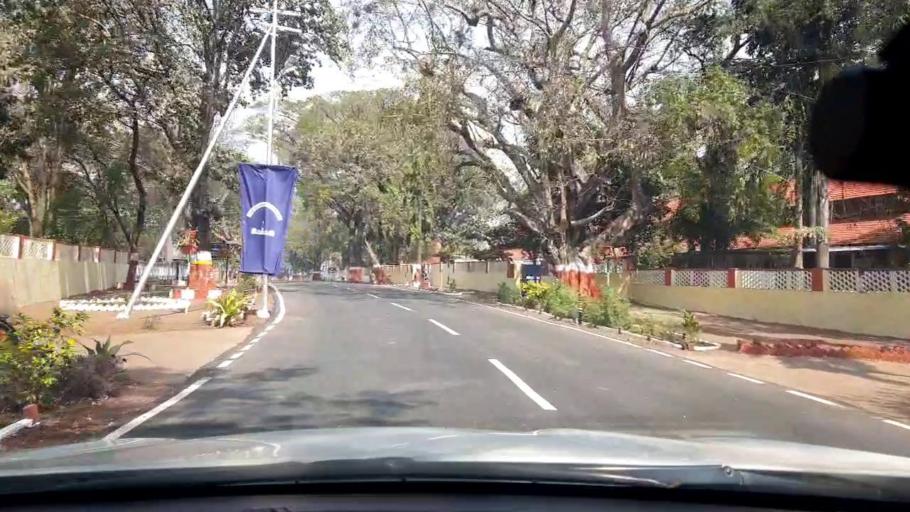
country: IN
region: Maharashtra
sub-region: Pune Division
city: Khadki
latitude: 18.5482
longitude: 73.8667
